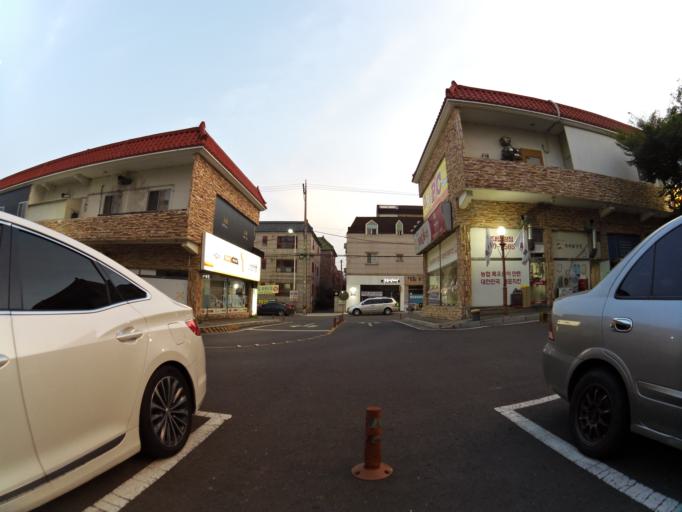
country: KR
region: Gyeongsangbuk-do
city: Gyeongsan-si
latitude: 35.8412
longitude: 128.7542
